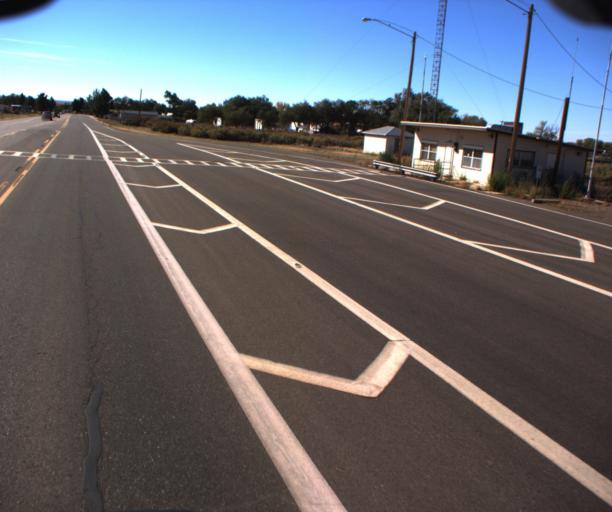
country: US
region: Arizona
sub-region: Coconino County
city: Fredonia
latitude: 36.9603
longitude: -112.5270
